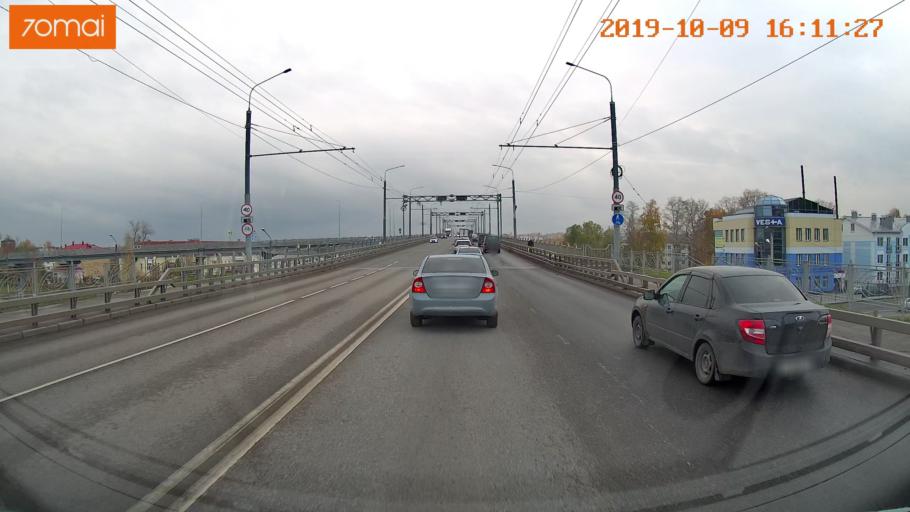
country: RU
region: Kostroma
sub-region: Kostromskoy Rayon
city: Kostroma
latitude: 57.7572
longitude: 40.9456
